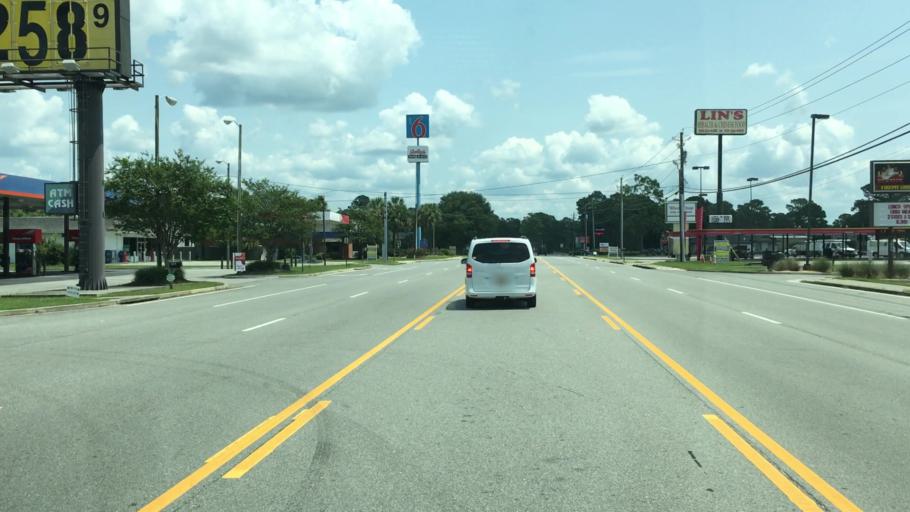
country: US
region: Georgia
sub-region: Lowndes County
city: Valdosta
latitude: 30.6816
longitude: -83.2193
